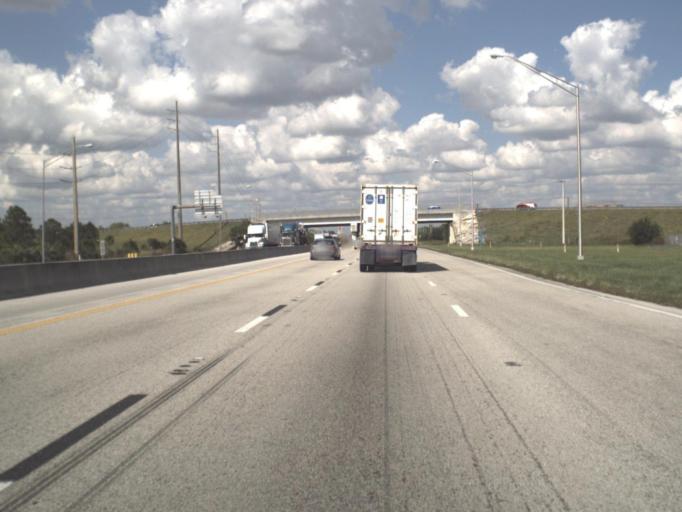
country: US
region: Florida
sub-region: Martin County
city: Palm City
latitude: 27.1595
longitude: -80.3033
